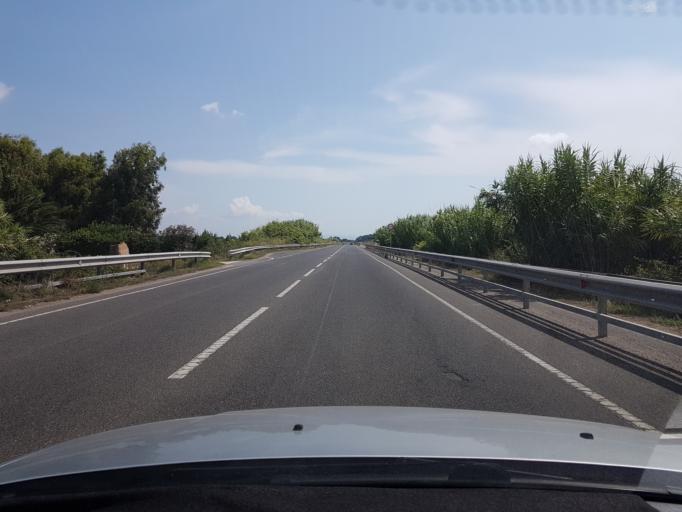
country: IT
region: Sardinia
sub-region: Provincia di Oristano
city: Solanas
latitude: 39.9156
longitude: 8.5474
